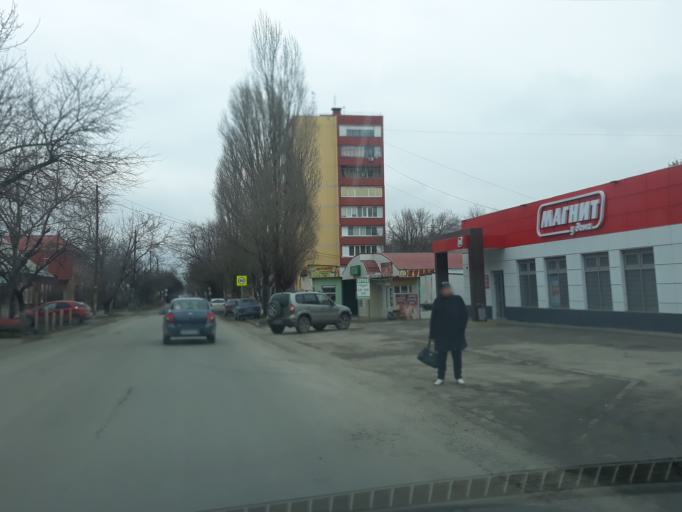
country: RU
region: Rostov
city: Taganrog
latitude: 47.2584
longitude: 38.9001
